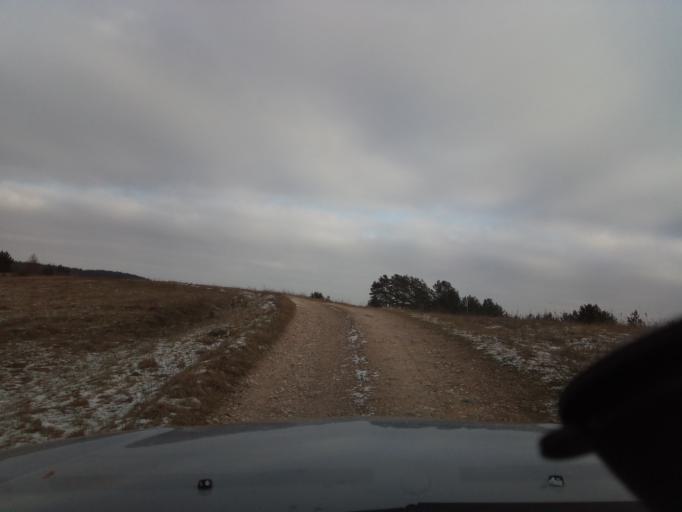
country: LT
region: Alytaus apskritis
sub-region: Alytaus rajonas
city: Daugai
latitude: 54.3329
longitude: 24.2868
